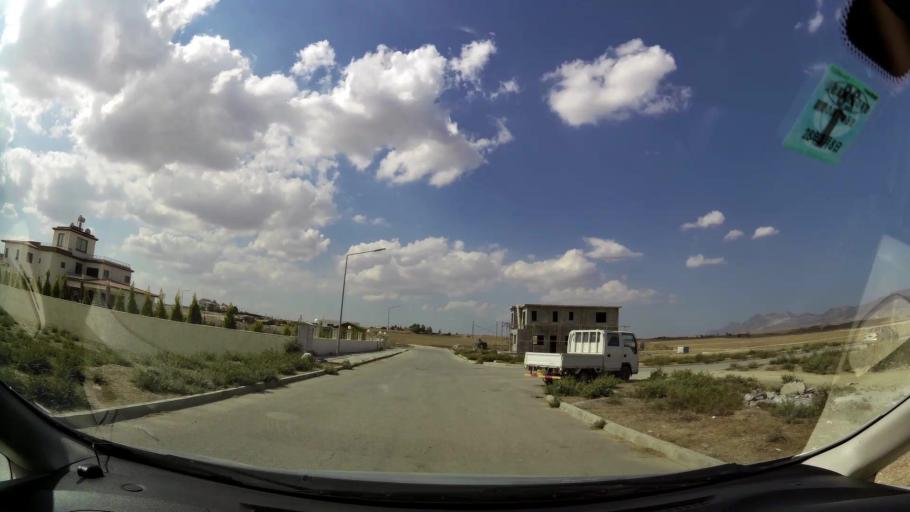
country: CY
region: Lefkosia
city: Nicosia
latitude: 35.2155
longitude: 33.2899
